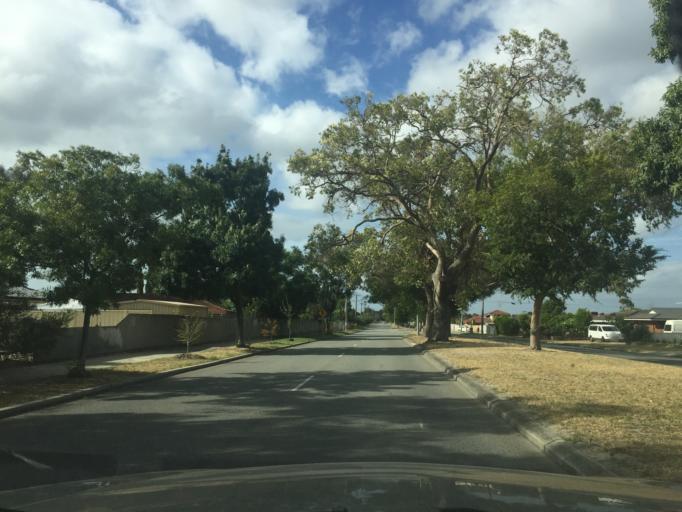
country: AU
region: Western Australia
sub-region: Canning
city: Willetton
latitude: -32.0471
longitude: 115.9040
